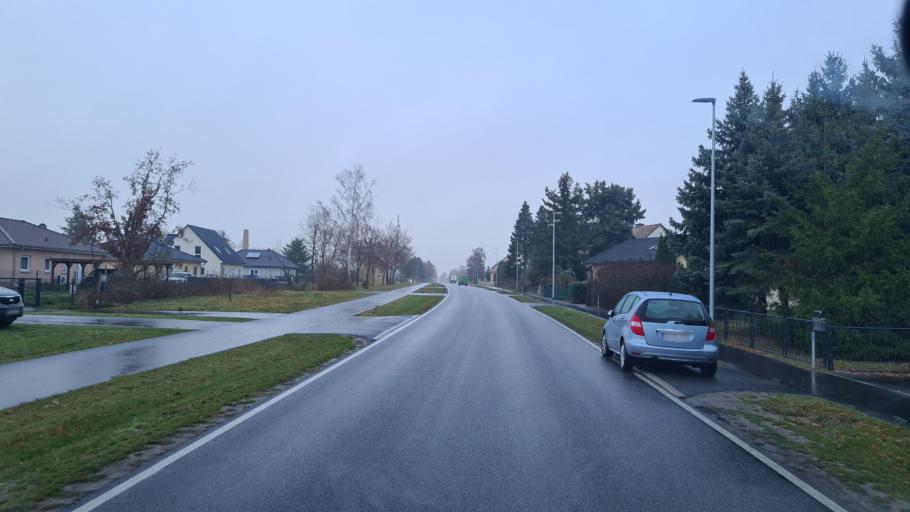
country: DE
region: Brandenburg
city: Gross Kreutz
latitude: 52.3716
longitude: 12.7647
